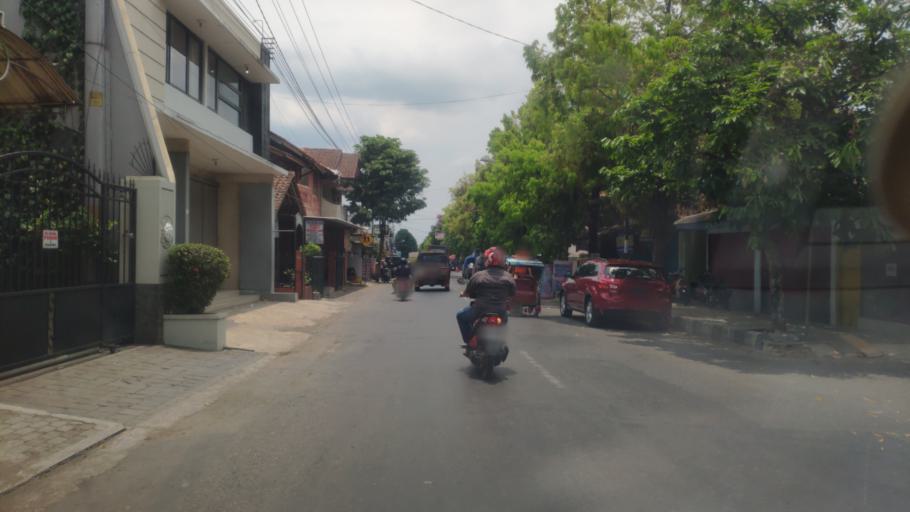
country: ID
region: Central Java
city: Wonosobo
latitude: -7.3974
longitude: 109.6999
